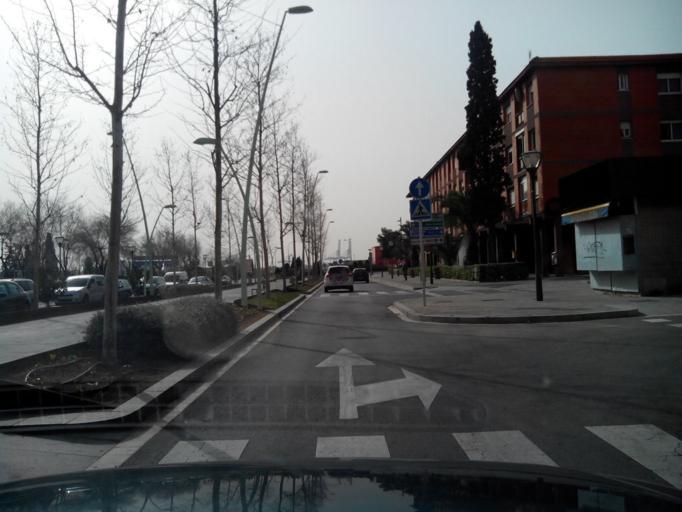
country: ES
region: Catalonia
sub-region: Provincia de Tarragona
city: Constanti
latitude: 41.1166
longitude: 1.2105
